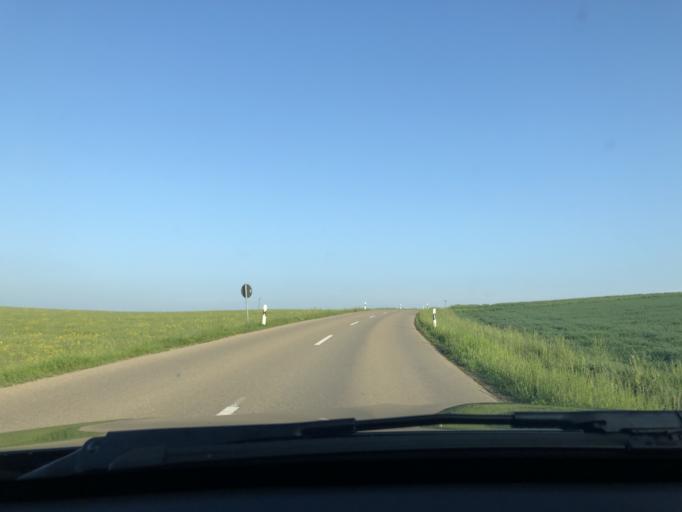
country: DE
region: Bavaria
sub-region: Upper Bavaria
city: Schweitenkirchen
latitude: 48.4919
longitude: 11.6171
